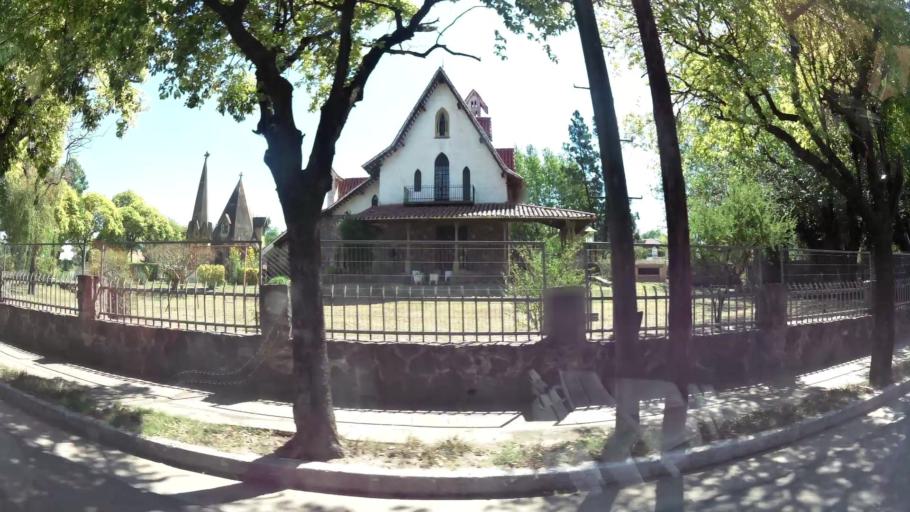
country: AR
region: Cordoba
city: Villa Allende
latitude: -31.2910
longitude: -64.2972
